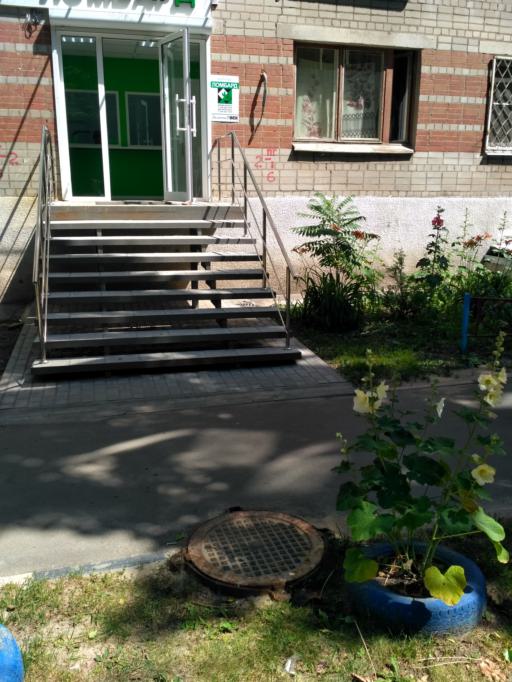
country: RU
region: Voronezj
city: Voronezh
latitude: 51.6506
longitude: 39.1283
